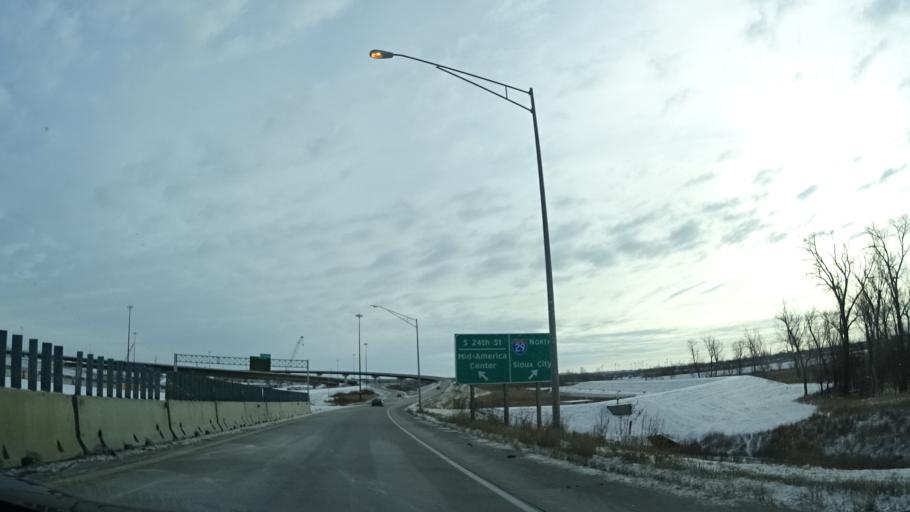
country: US
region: Nebraska
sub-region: Douglas County
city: Omaha
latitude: 41.2317
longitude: -95.9046
